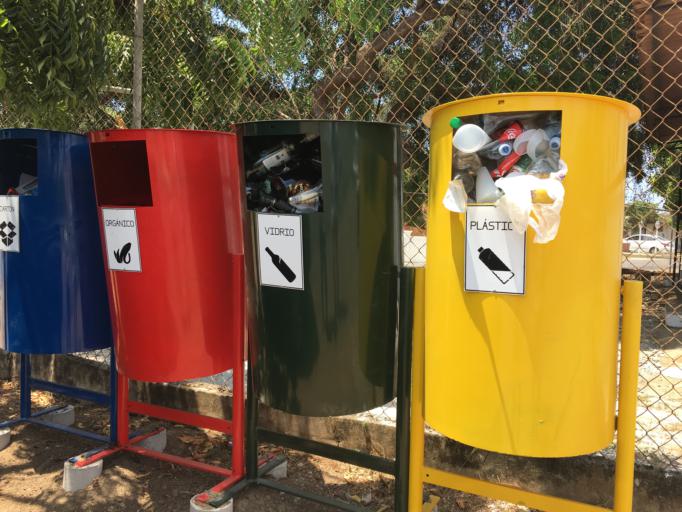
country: PA
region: Los Santos
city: Pedasi
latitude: 7.5345
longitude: -80.0261
